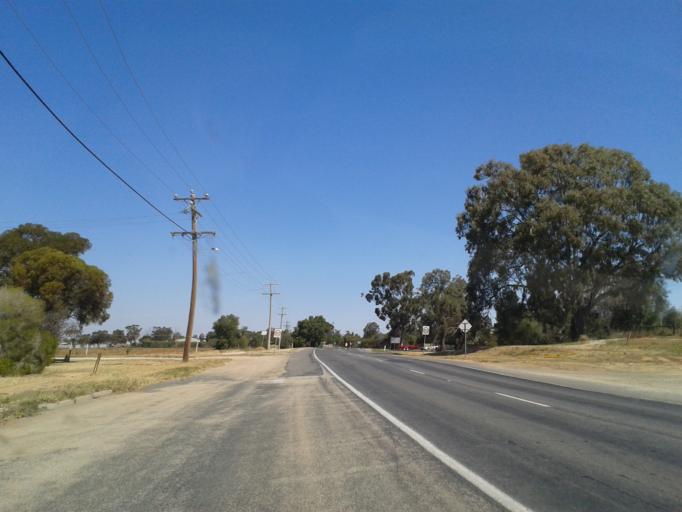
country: AU
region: Victoria
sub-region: Swan Hill
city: Swan Hill
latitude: -35.1761
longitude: 143.3774
